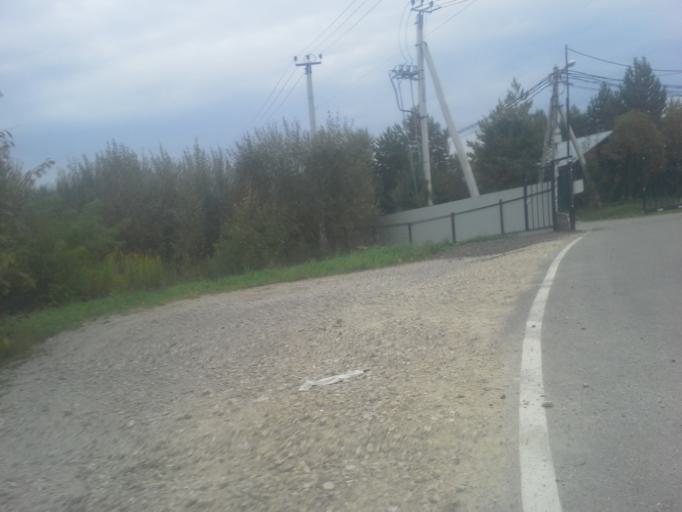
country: RU
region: Moskovskaya
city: Kievskij
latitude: 55.3513
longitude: 36.9064
